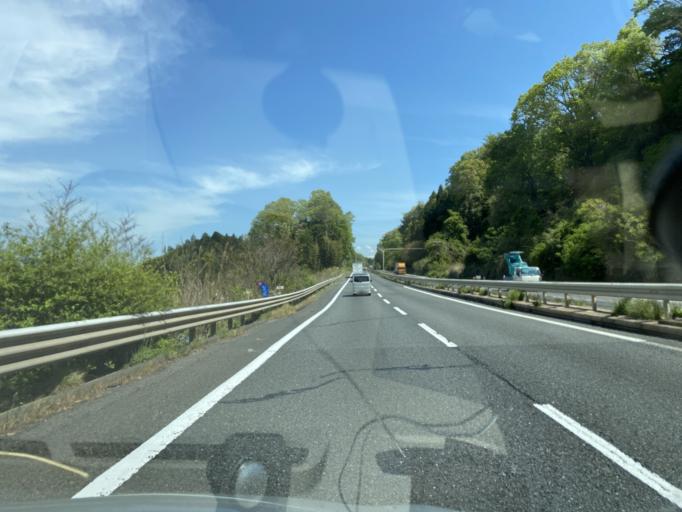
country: JP
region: Mie
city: Nabari
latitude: 34.6630
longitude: 136.0331
